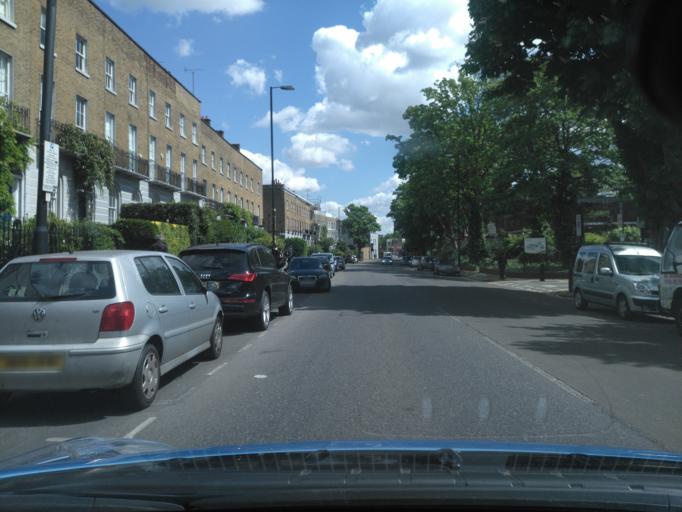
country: GB
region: England
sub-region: Greater London
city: Islington
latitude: 51.5469
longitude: -0.0897
